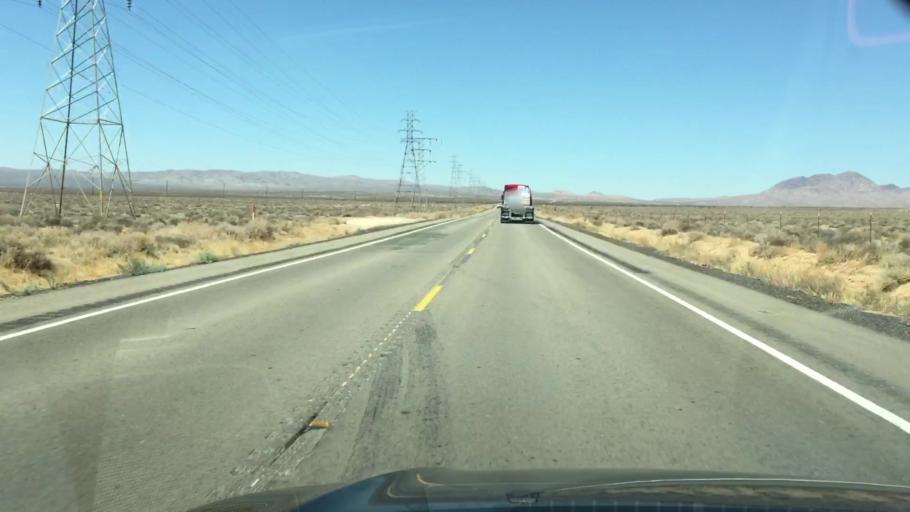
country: US
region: California
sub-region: Kern County
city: Boron
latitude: 35.2115
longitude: -117.6027
